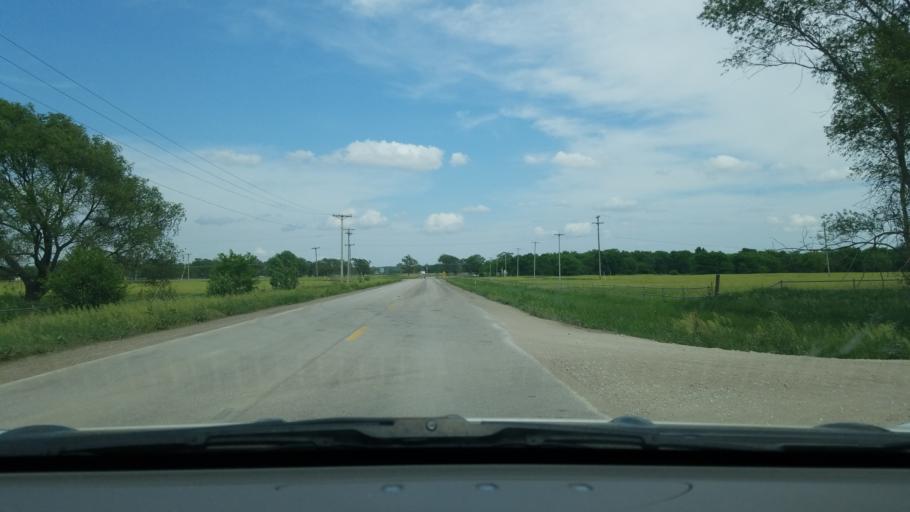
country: US
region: Nebraska
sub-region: Saunders County
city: Ashland
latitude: 41.0597
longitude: -96.3399
